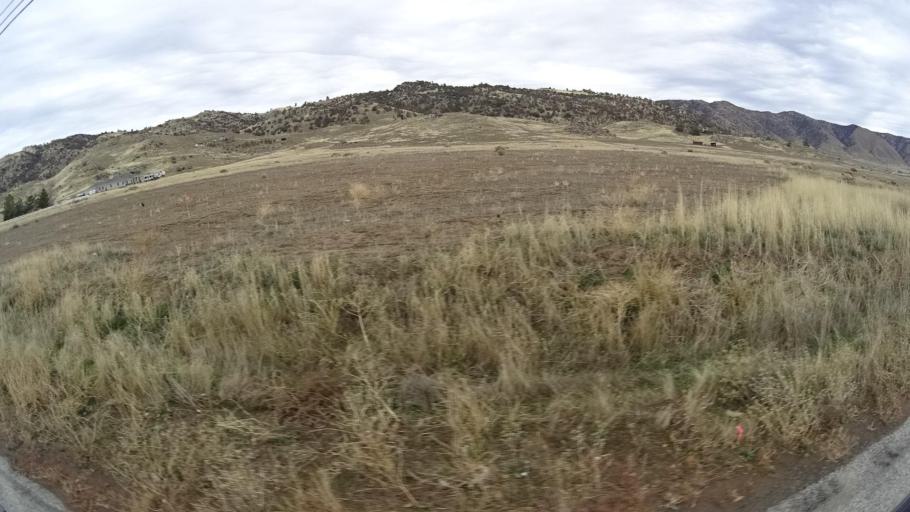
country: US
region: California
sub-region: Kern County
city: Bear Valley Springs
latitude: 35.1234
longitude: -118.6104
